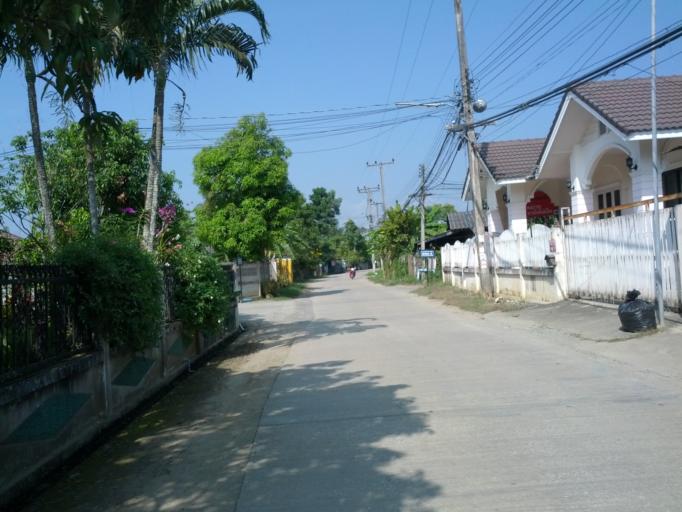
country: TH
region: Chiang Mai
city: San Kamphaeng
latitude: 18.7786
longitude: 99.0975
